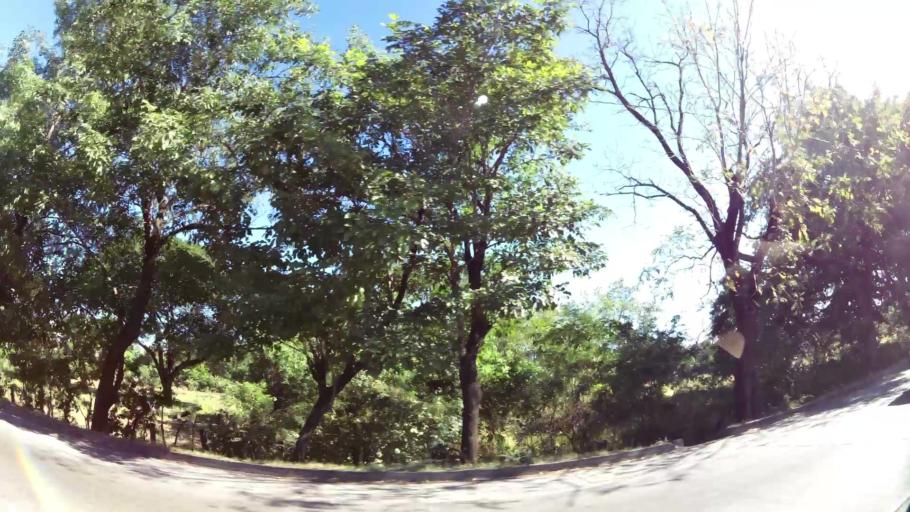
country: SV
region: San Miguel
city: San Miguel
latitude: 13.4589
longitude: -88.1468
